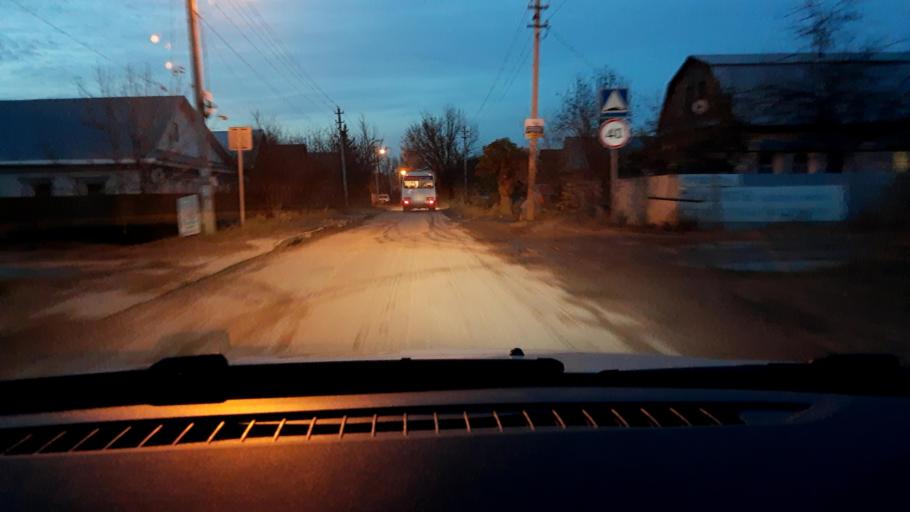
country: RU
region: Nizjnij Novgorod
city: Neklyudovo
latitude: 56.4094
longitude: 43.9803
